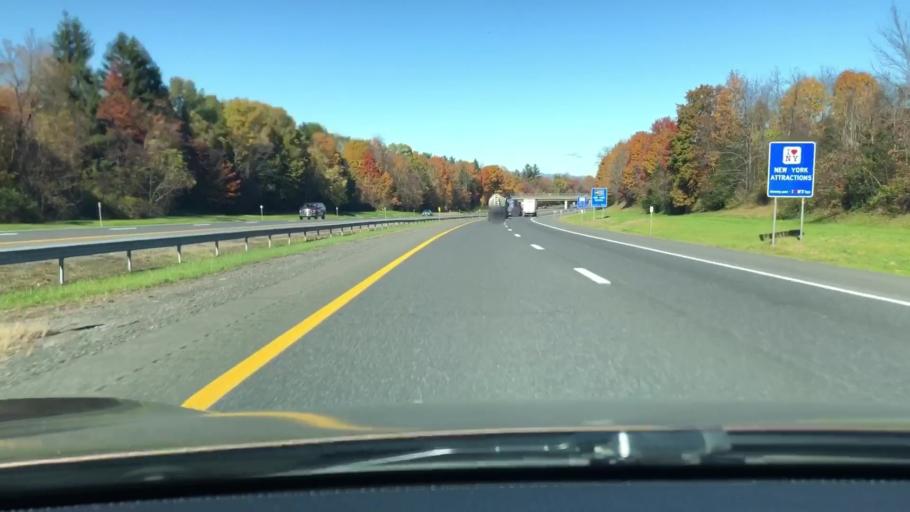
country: US
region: New York
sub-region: Ulster County
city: Clintondale
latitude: 41.6965
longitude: -74.0795
